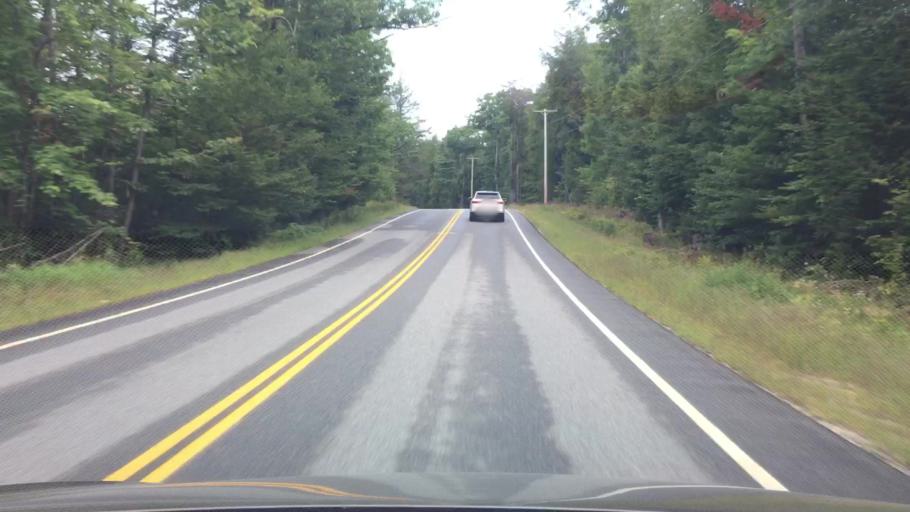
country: US
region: Maine
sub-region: Oxford County
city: Hartford
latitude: 44.3601
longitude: -70.3099
